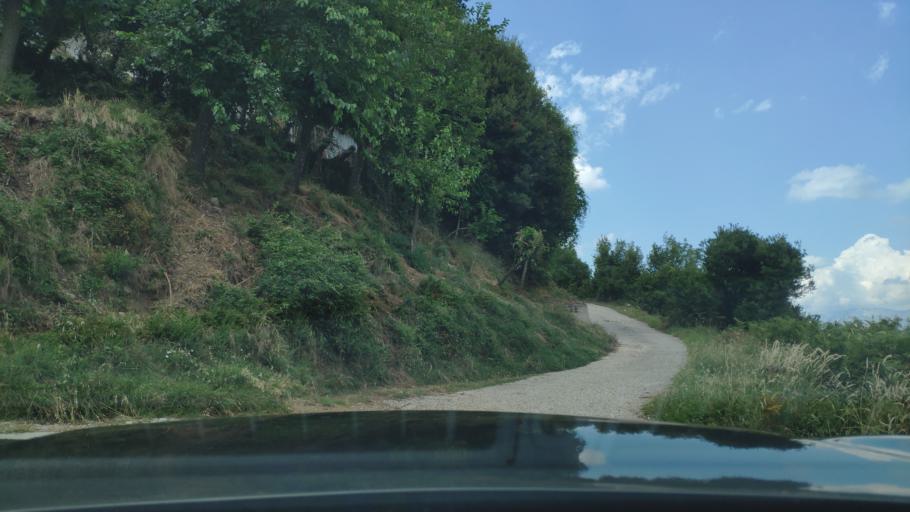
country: GR
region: Epirus
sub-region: Nomos Artas
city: Agios Dimitrios
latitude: 39.3203
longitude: 20.9997
